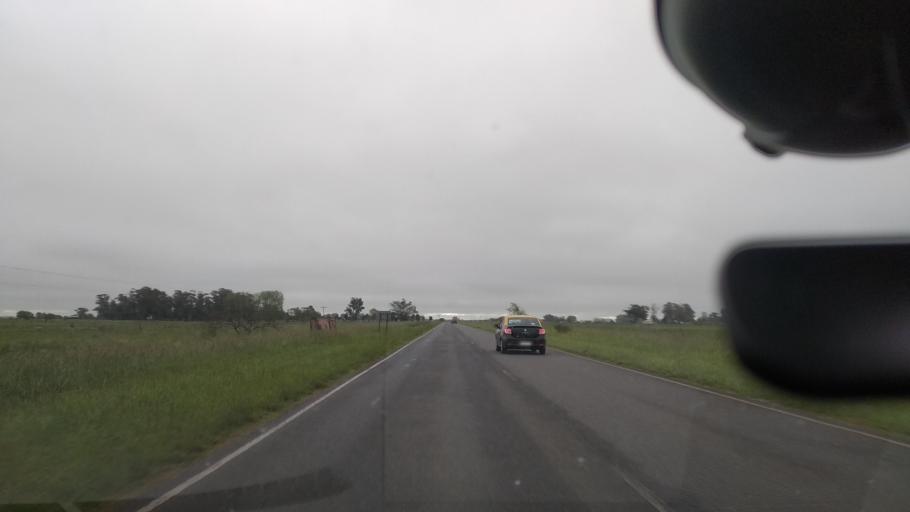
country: AR
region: Buenos Aires
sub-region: Partido de Magdalena
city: Magdalena
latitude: -35.2266
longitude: -57.7236
